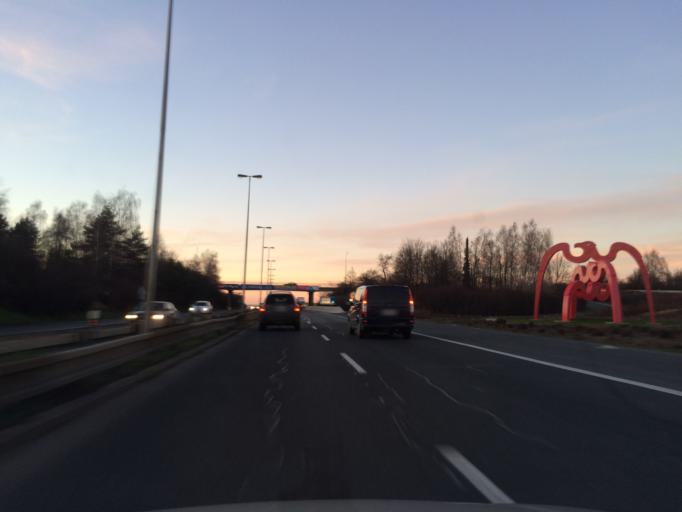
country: CZ
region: Central Bohemia
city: Tuchomerice
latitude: 50.1140
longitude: 14.2865
